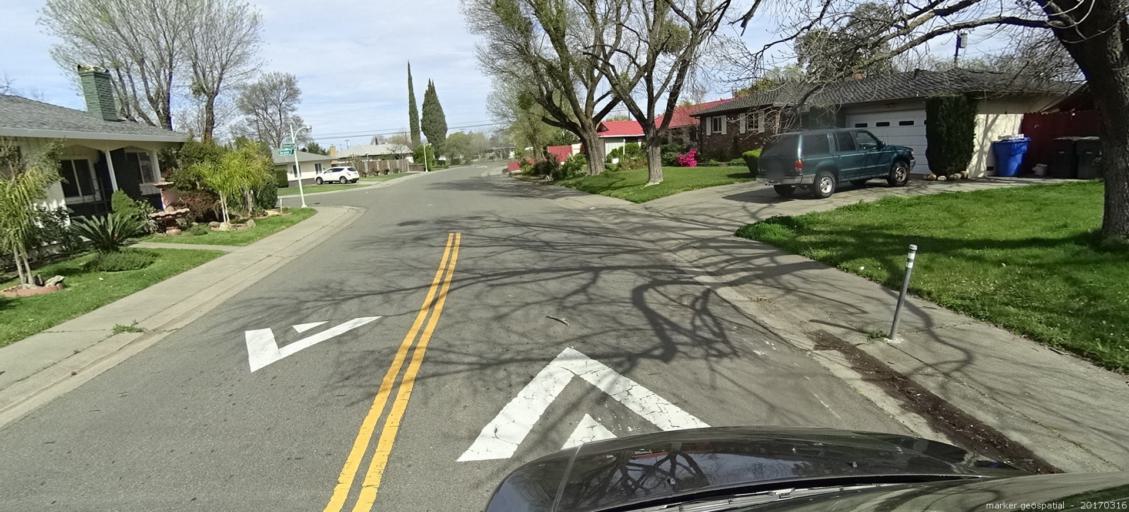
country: US
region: California
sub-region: Sacramento County
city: Parkway
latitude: 38.5012
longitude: -121.4852
